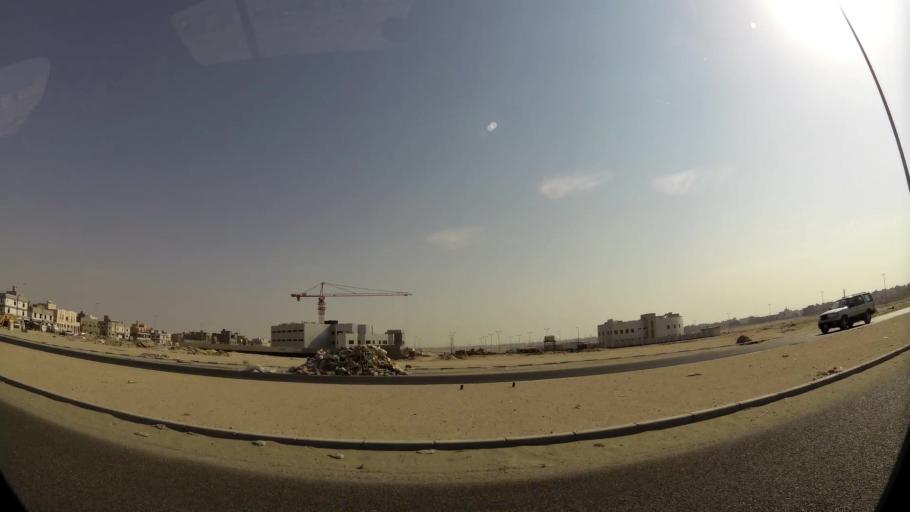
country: KW
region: Al Ahmadi
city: Al Wafrah
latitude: 28.7805
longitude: 48.0518
